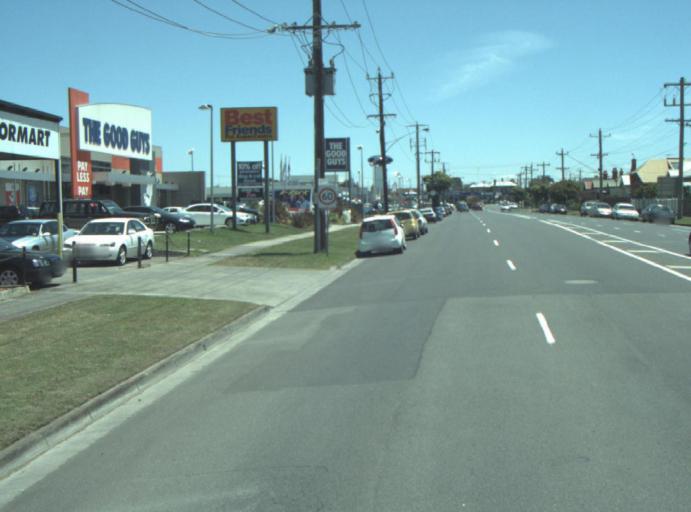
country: AU
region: Victoria
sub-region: Greater Geelong
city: Geelong
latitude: -38.1617
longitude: 144.3540
